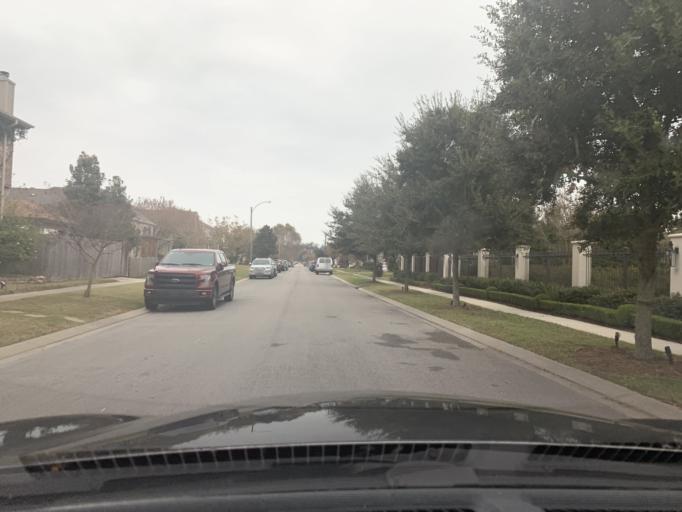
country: US
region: Louisiana
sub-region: Jefferson Parish
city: Metairie
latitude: 30.0122
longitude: -90.1059
